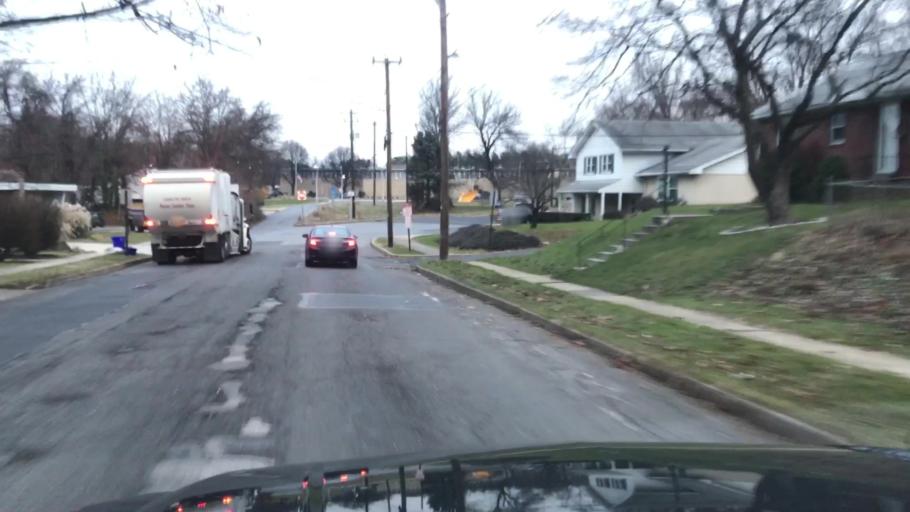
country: US
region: Pennsylvania
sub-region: Dauphin County
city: Harrisburg
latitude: 40.2773
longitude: -76.8695
